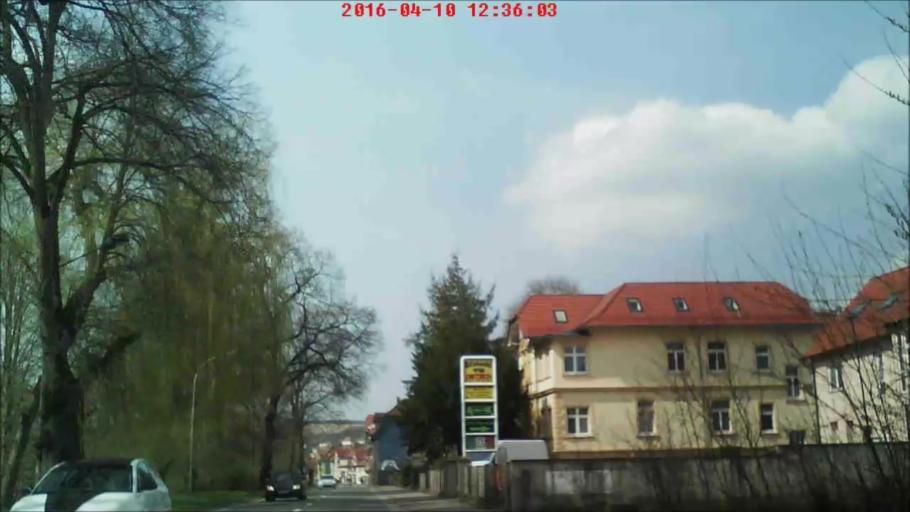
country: DE
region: Thuringia
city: Schmalkalden
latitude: 50.7191
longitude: 10.4615
